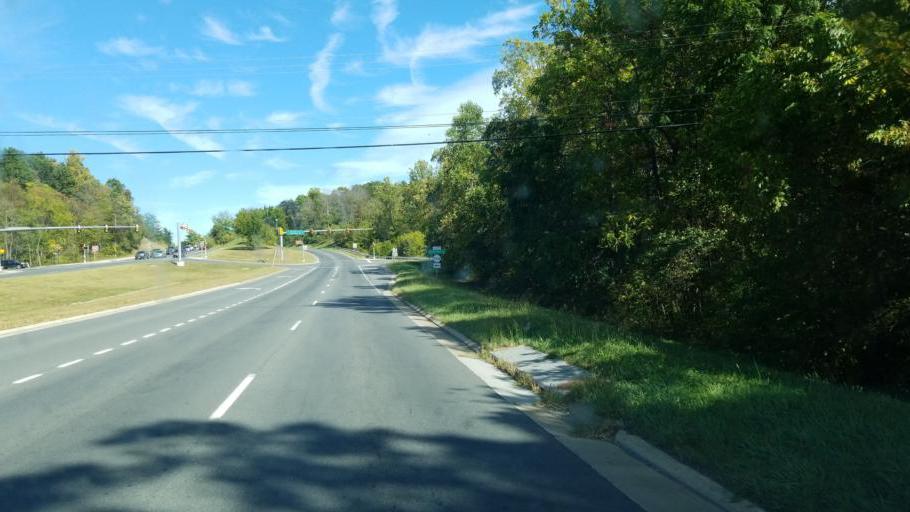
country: US
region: Virginia
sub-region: Warren County
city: Front Royal
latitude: 38.9045
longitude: -78.2066
